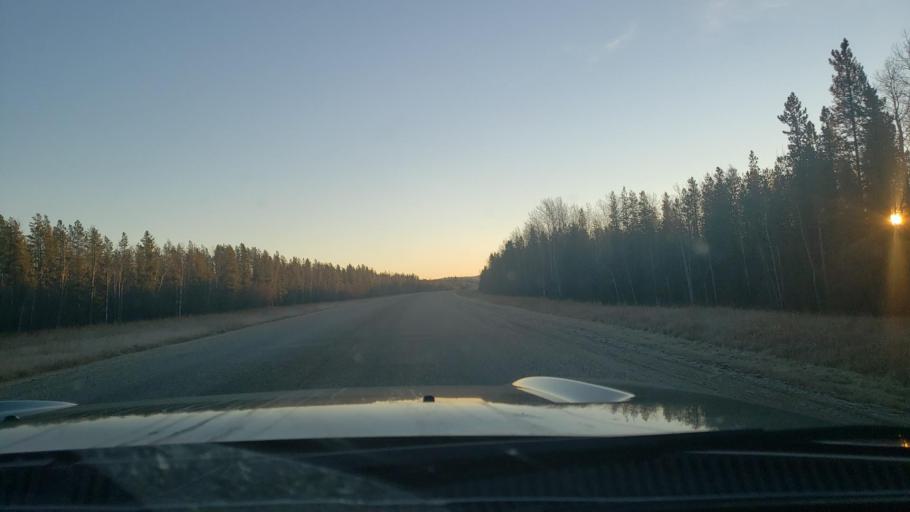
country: CA
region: Yukon
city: Watson Lake
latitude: 59.9338
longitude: -128.2955
